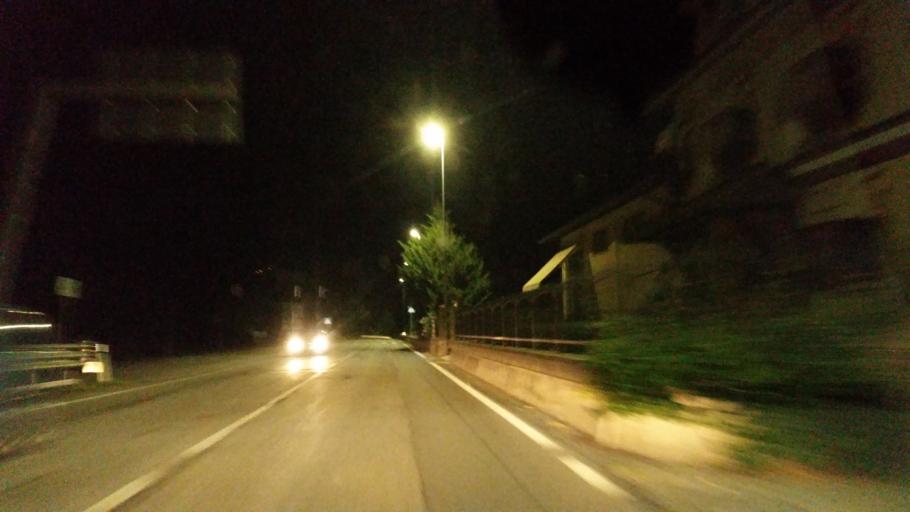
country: IT
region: Piedmont
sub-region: Provincia di Cuneo
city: Camerana
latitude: 44.4387
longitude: 8.1517
